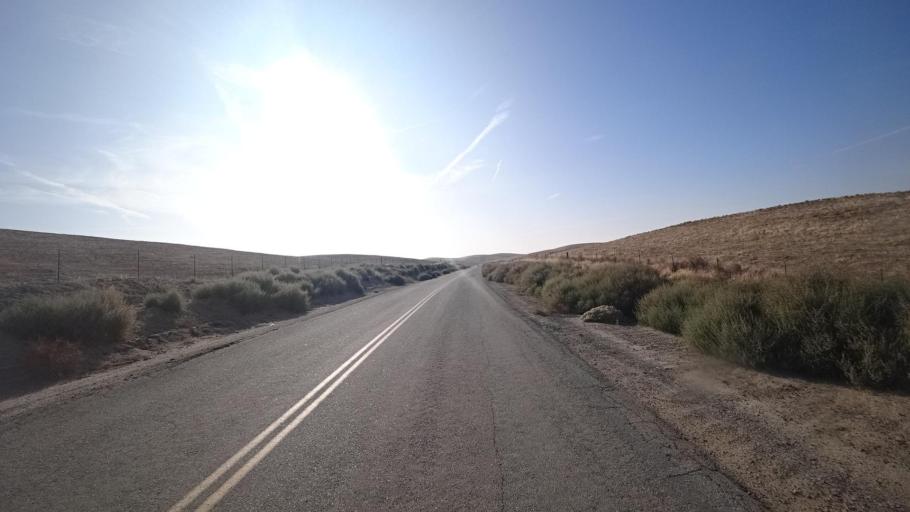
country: US
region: California
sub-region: Tulare County
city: Richgrove
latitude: 35.6268
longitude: -119.0308
